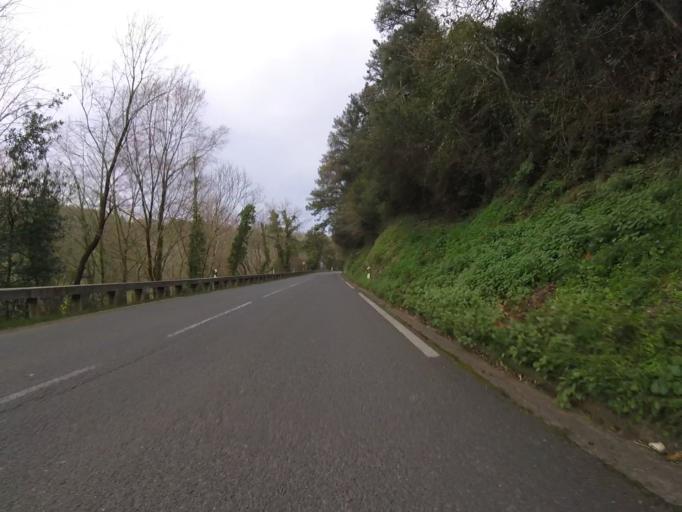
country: ES
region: Basque Country
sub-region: Provincia de Guipuzcoa
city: Aizarnazabal
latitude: 43.2703
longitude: -2.2320
